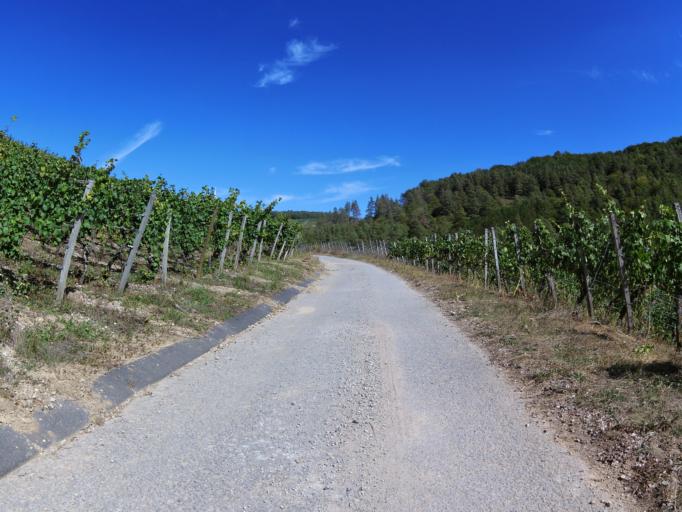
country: DE
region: Bavaria
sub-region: Regierungsbezirk Unterfranken
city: Thungersheim
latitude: 49.8669
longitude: 9.8630
